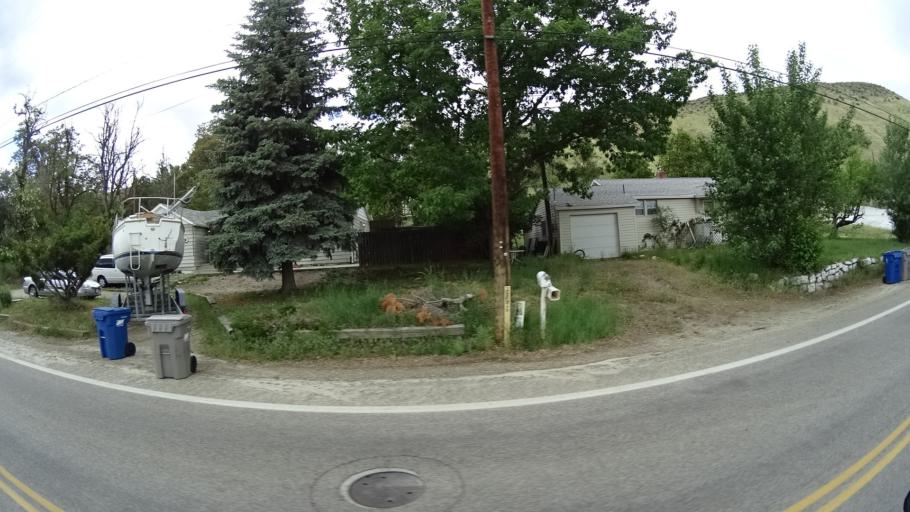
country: US
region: Idaho
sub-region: Ada County
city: Garden City
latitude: 43.6733
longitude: -116.2580
